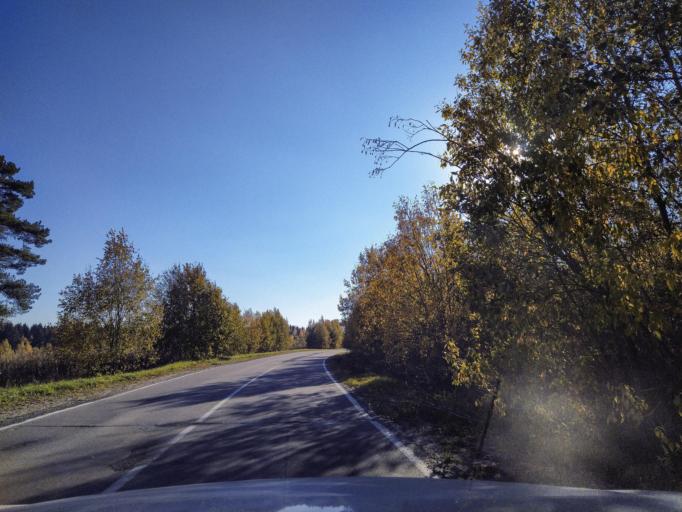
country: RU
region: Leningrad
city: Siverskiy
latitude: 59.3140
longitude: 30.0331
